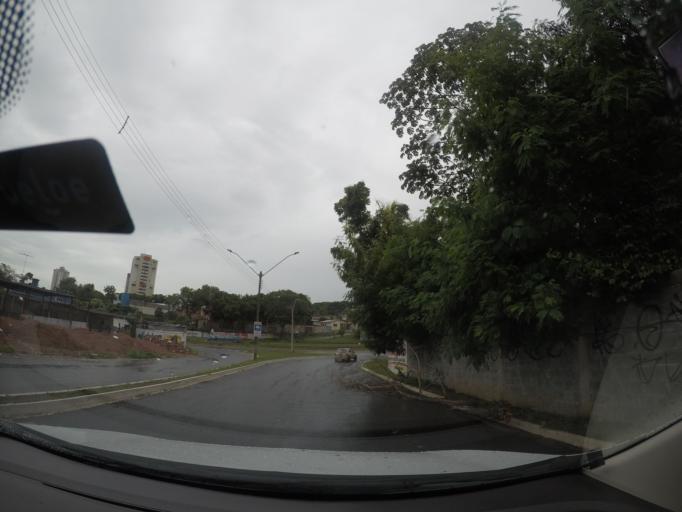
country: BR
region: Goias
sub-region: Goiania
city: Goiania
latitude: -16.6887
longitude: -49.2450
